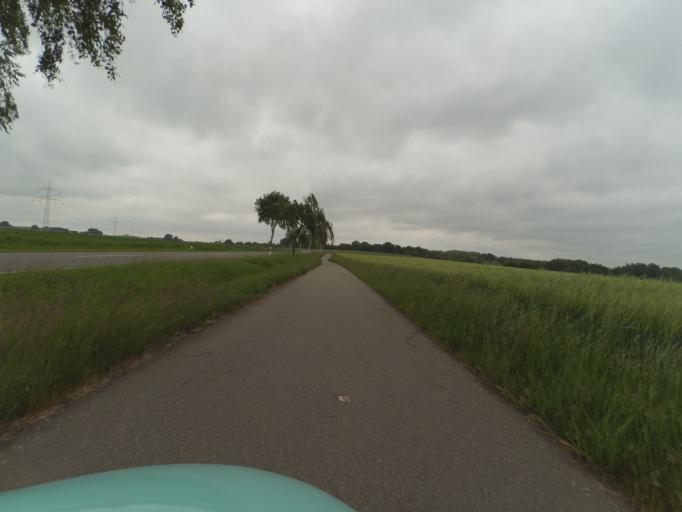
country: DE
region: Lower Saxony
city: Wendeburg
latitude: 52.3513
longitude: 10.3620
